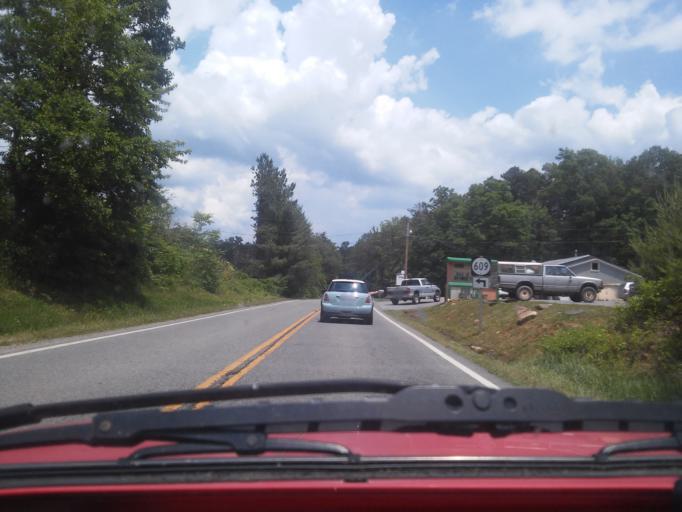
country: US
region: Virginia
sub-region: Craig County
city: New Castle
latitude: 37.5251
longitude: -80.0748
